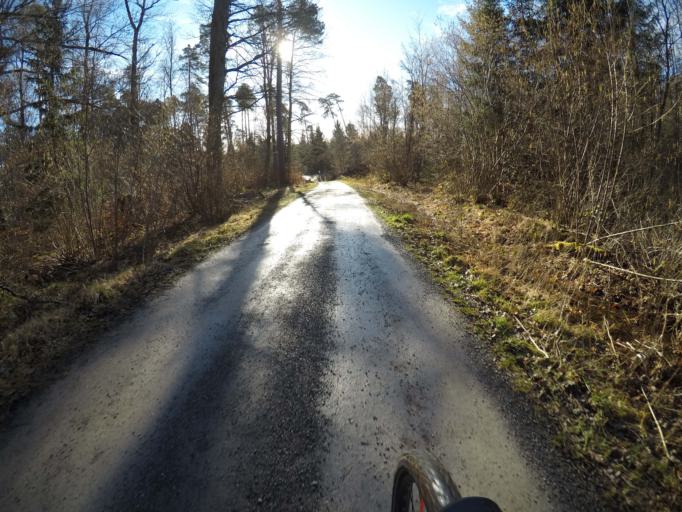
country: DE
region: Baden-Wuerttemberg
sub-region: Regierungsbezirk Stuttgart
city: Steinenbronn
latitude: 48.6889
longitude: 9.1088
